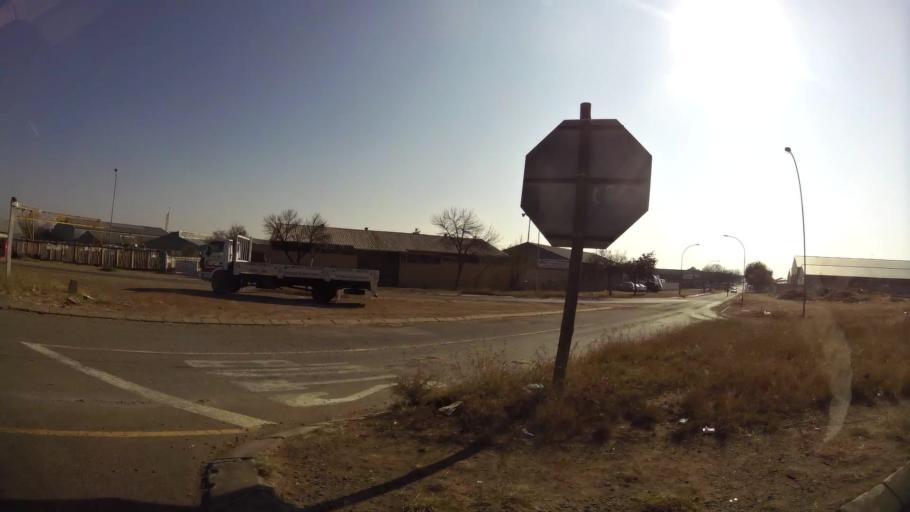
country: ZA
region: Orange Free State
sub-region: Mangaung Metropolitan Municipality
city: Bloemfontein
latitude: -29.1734
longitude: 26.2270
